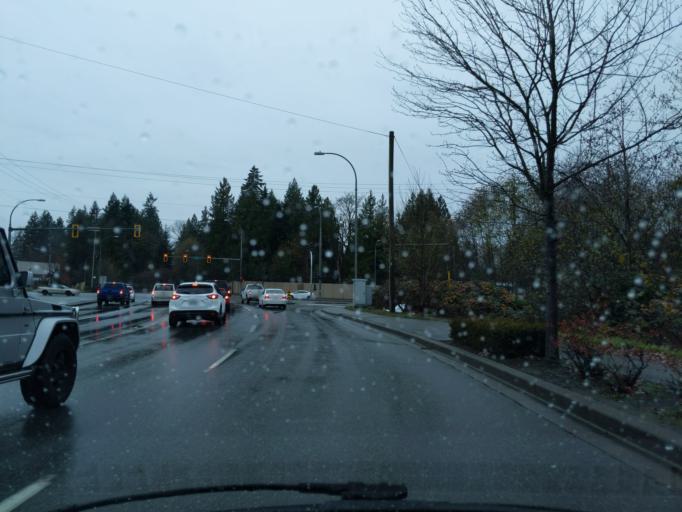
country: CA
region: British Columbia
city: Walnut Grove
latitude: 49.1663
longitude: -122.6670
